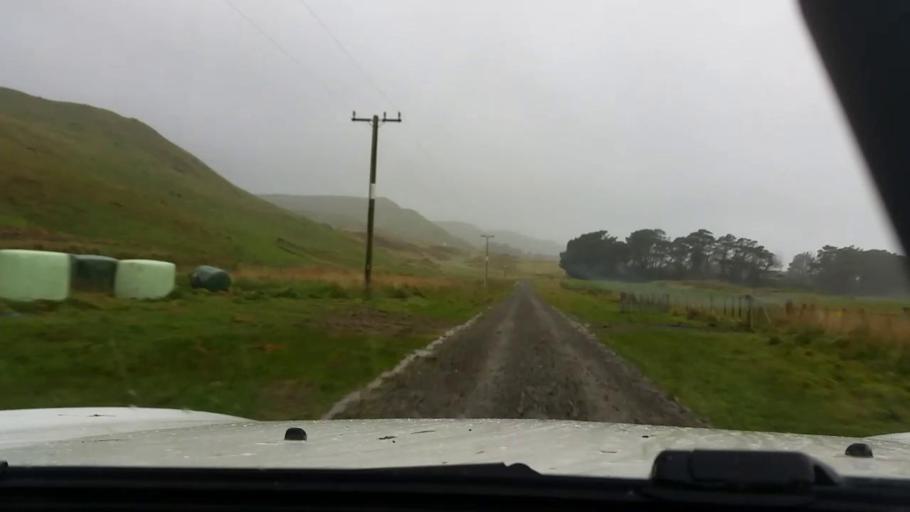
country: NZ
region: Wellington
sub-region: Masterton District
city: Masterton
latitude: -41.2547
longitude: 175.9093
